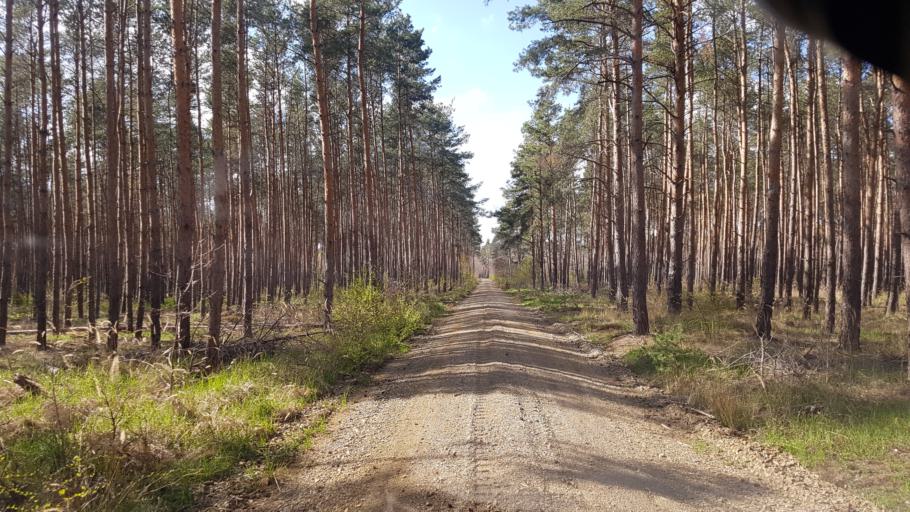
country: DE
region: Brandenburg
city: Muhlberg
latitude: 51.4795
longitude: 13.2875
